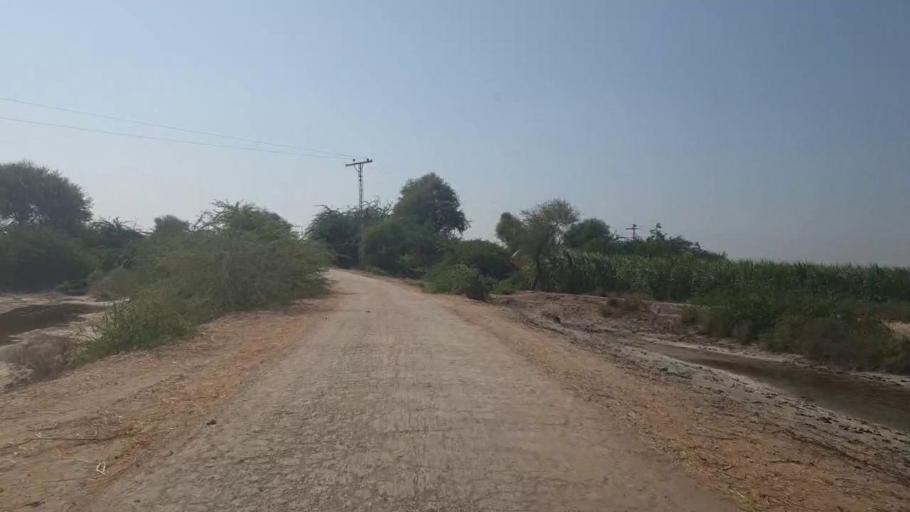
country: PK
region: Sindh
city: Badin
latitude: 24.6463
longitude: 68.9161
